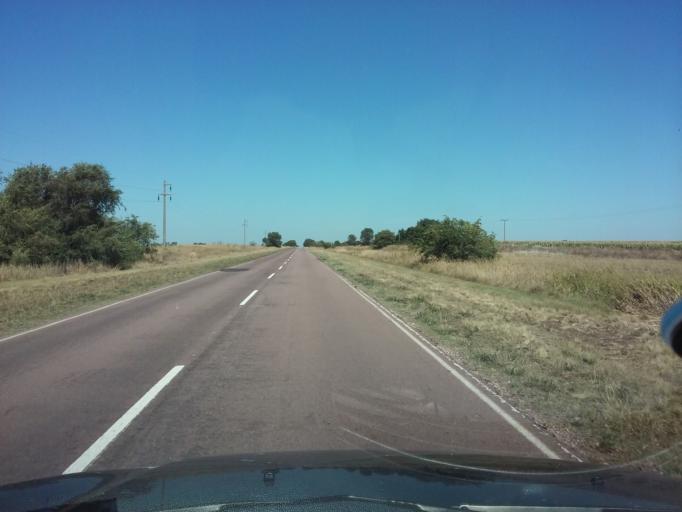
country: AR
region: La Pampa
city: Uriburu
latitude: -36.3981
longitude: -63.9430
